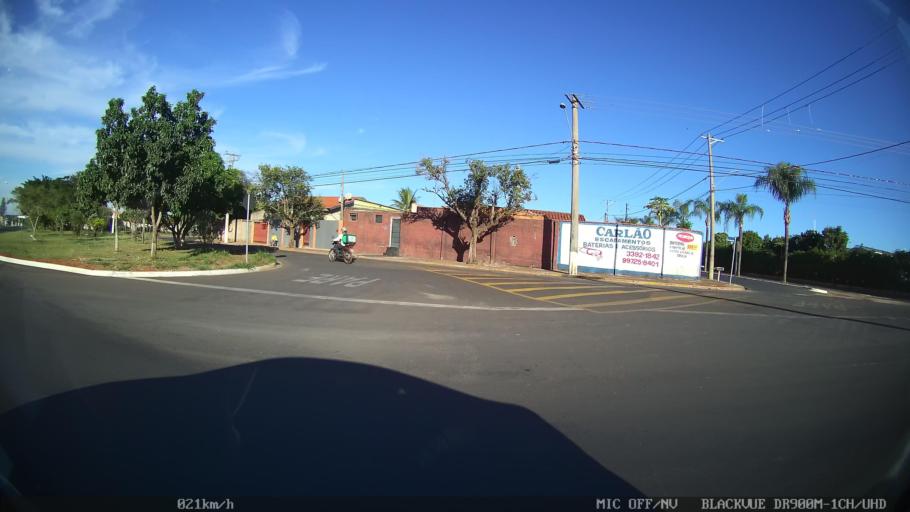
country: BR
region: Sao Paulo
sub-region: Americo Brasiliense
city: Americo Brasiliense
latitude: -21.7439
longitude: -48.1252
